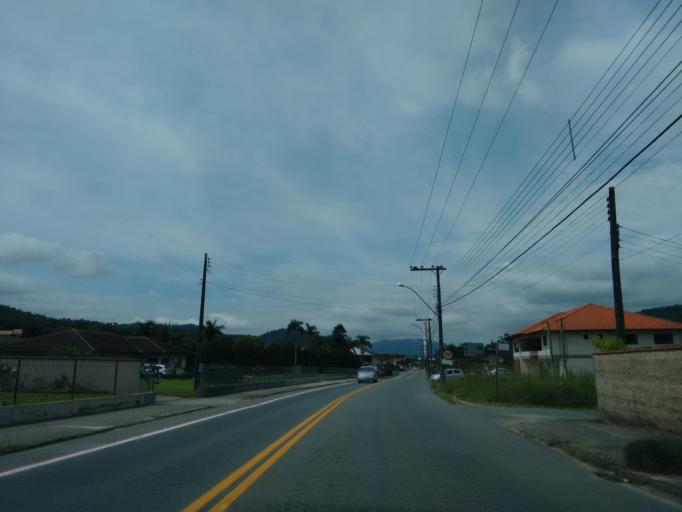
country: BR
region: Santa Catarina
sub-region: Pomerode
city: Pomerode
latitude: -26.6999
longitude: -49.1606
